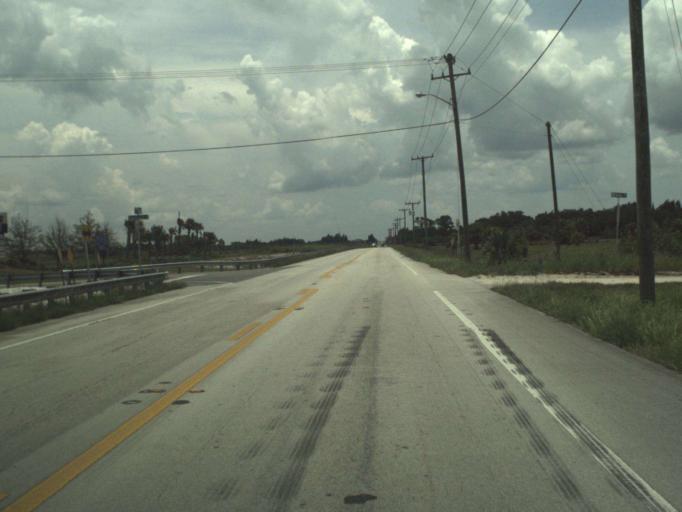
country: US
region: Florida
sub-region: Saint Lucie County
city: Fort Pierce South
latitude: 27.4252
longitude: -80.3991
